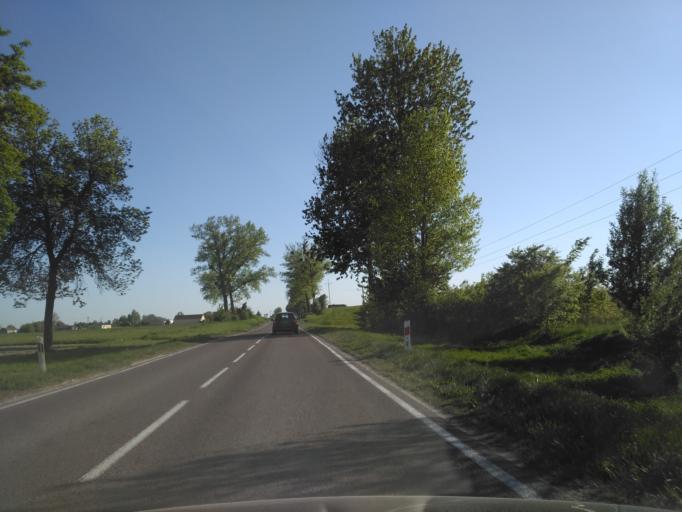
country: PL
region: Lublin Voivodeship
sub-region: Powiat swidnicki
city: Trawniki
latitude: 51.2104
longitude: 23.0708
